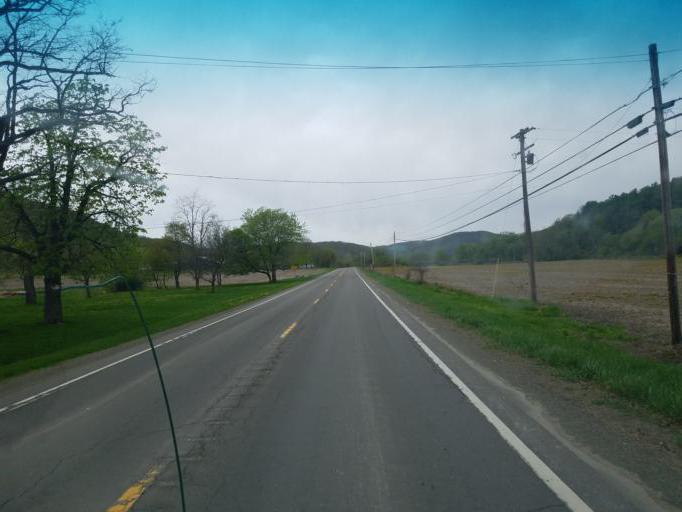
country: US
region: Pennsylvania
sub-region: Tioga County
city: Westfield
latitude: 41.9134
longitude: -77.5859
